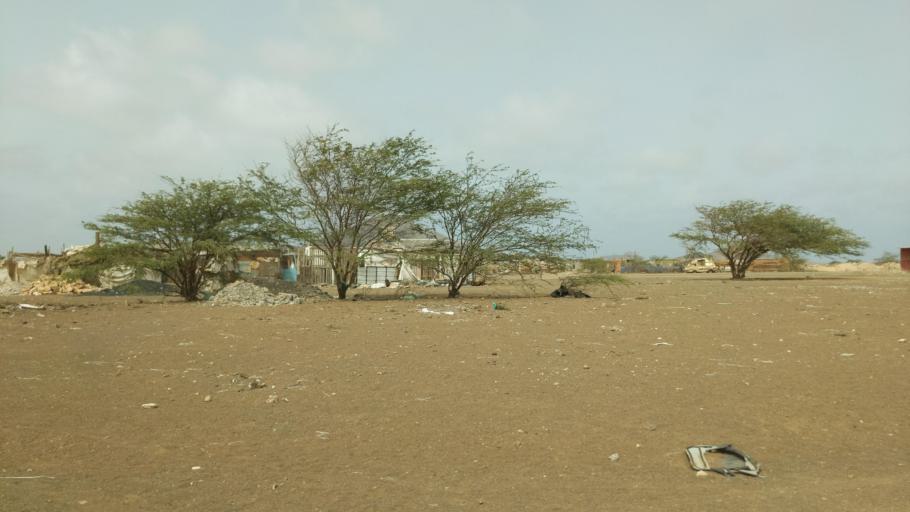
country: CV
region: Sal
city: Espargos
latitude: 16.7724
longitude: -22.9469
